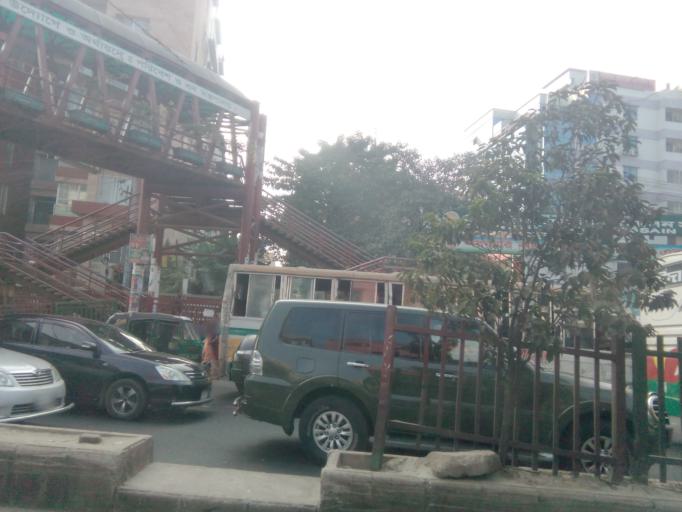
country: BD
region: Dhaka
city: Paltan
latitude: 23.8096
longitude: 90.4210
